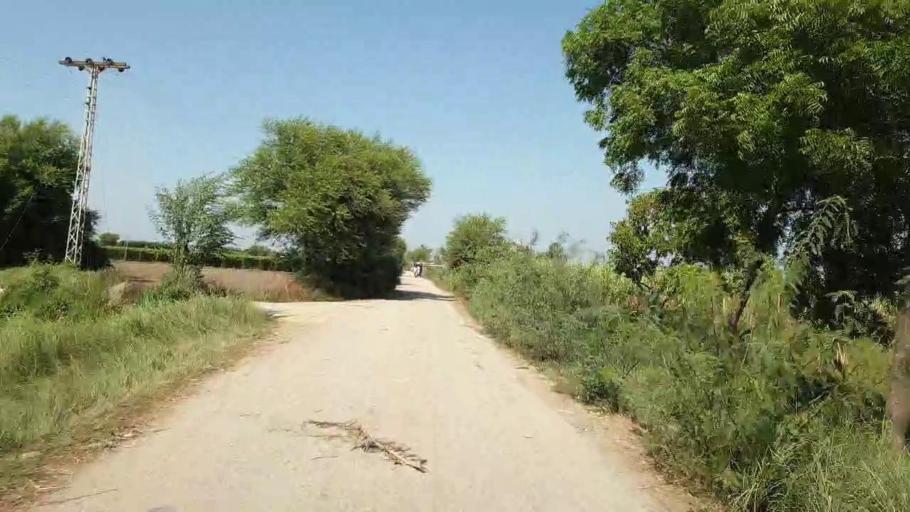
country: PK
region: Sindh
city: Tando Jam
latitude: 25.4952
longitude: 68.4637
